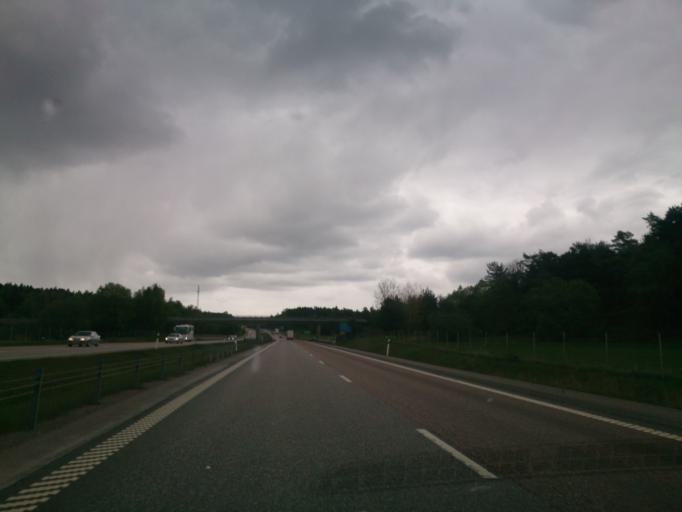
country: SE
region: Soedermanland
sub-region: Trosa Kommun
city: Vagnharad
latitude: 59.0118
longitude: 17.5447
